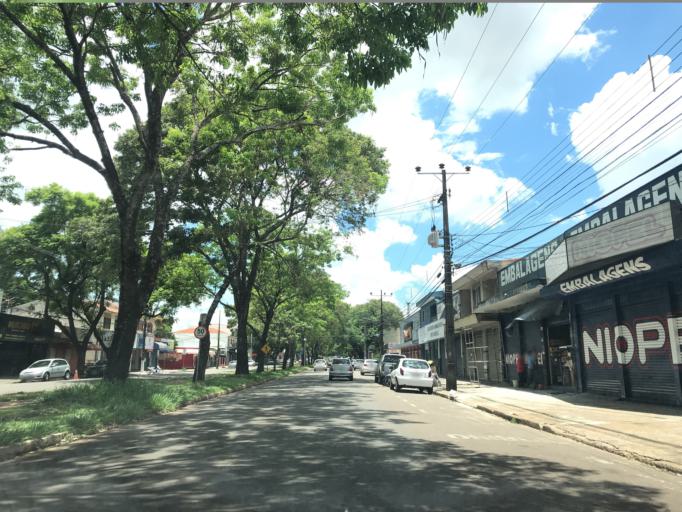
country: BR
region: Parana
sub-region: Maringa
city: Maringa
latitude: -23.3965
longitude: -51.9186
